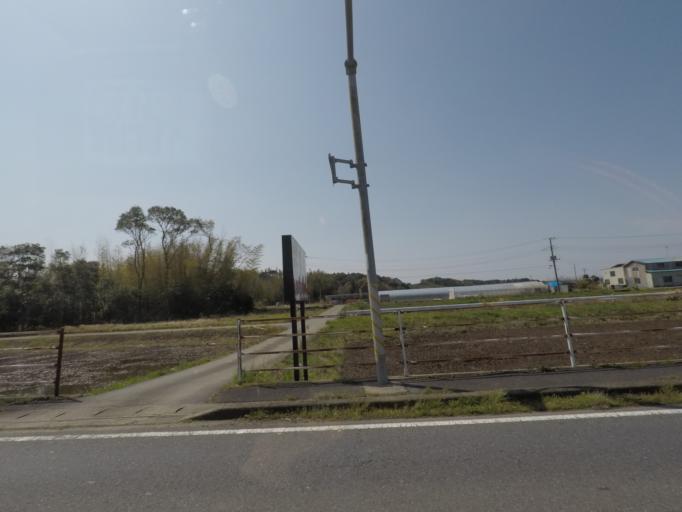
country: JP
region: Chiba
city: Narita
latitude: 35.8580
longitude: 140.2969
